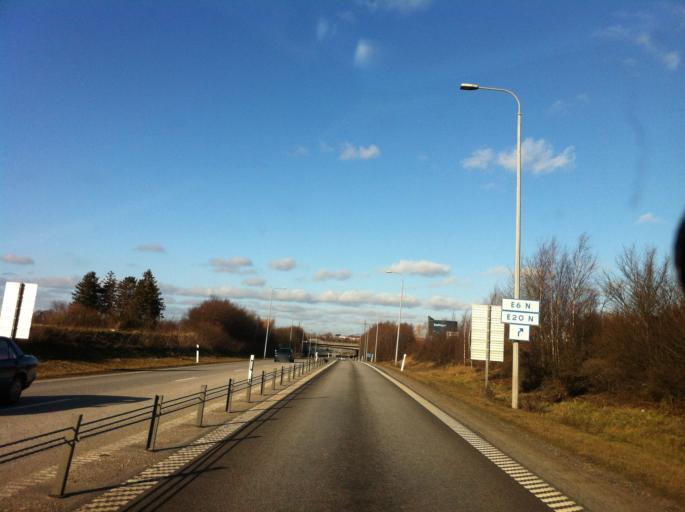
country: SE
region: Skane
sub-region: Svedala Kommun
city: Klagerup
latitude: 55.6157
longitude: 13.2623
